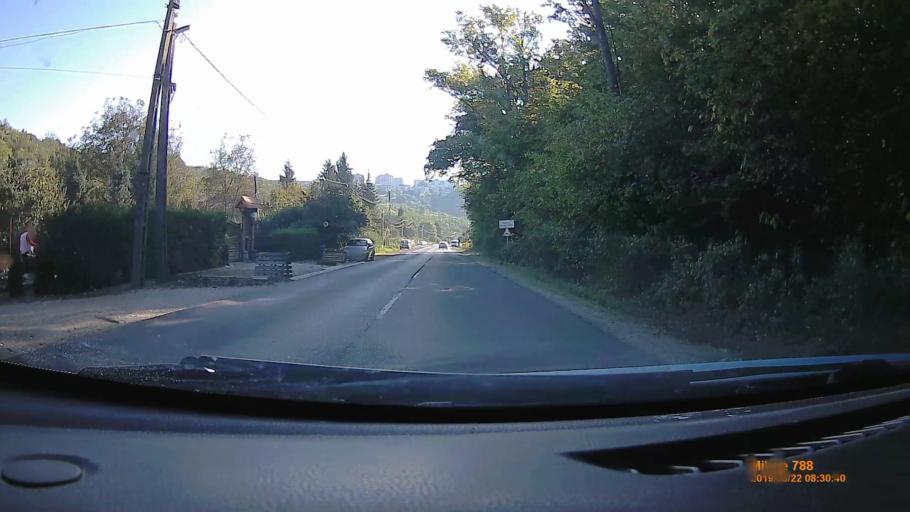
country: HU
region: Borsod-Abauj-Zemplen
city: Miskolc
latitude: 48.0906
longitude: 20.7589
